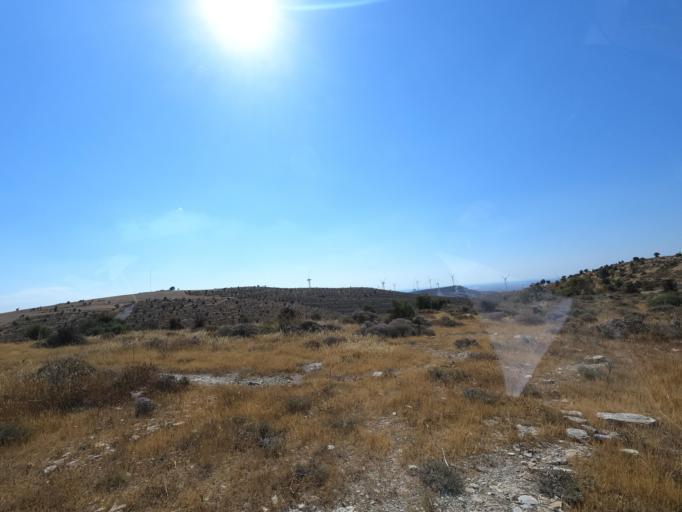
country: CY
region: Larnaka
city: Psevdas
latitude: 34.9684
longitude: 33.4787
